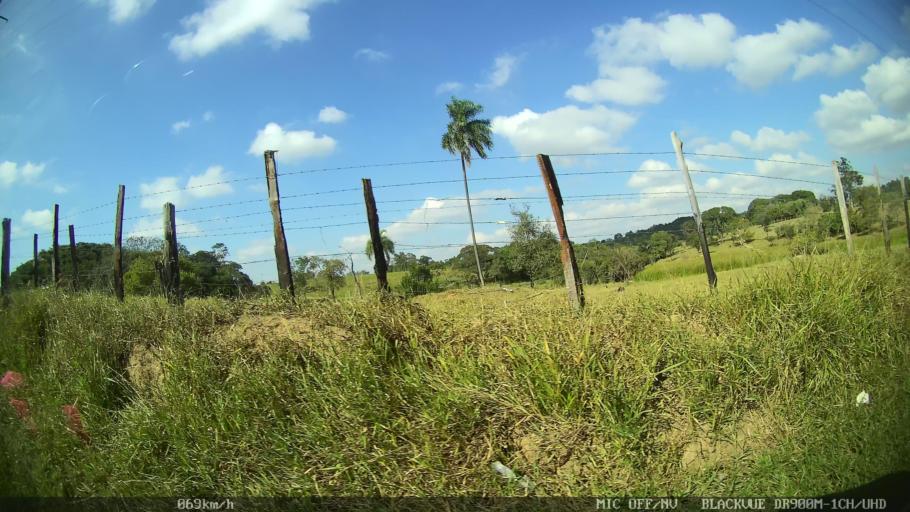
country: BR
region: Sao Paulo
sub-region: Indaiatuba
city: Indaiatuba
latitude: -22.9935
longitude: -47.1785
